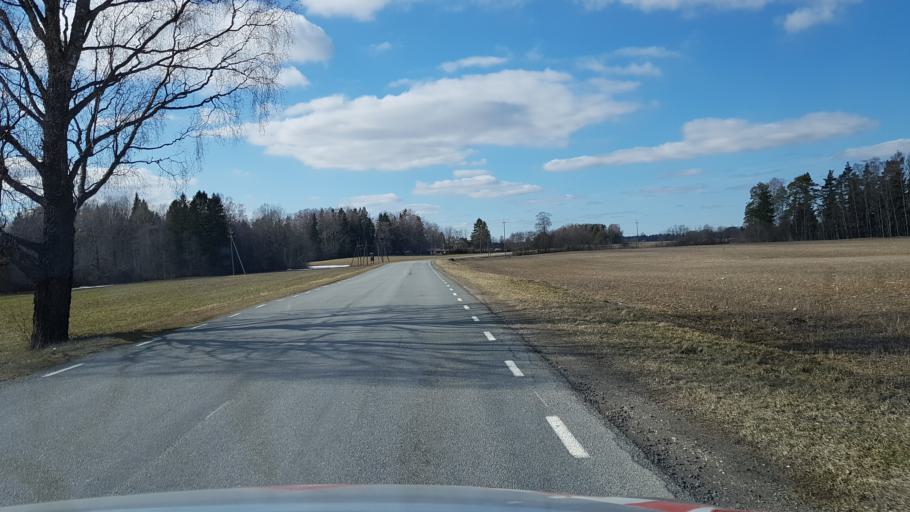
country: EE
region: Laeaene-Virumaa
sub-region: Tamsalu vald
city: Tamsalu
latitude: 59.1679
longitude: 26.0667
